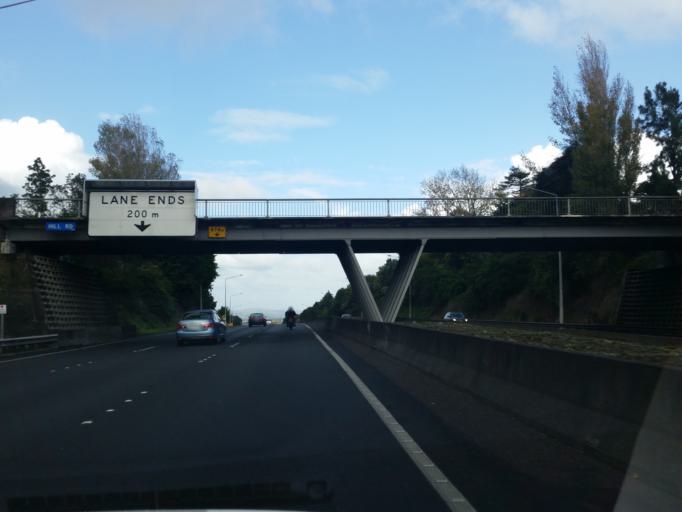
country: NZ
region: Auckland
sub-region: Auckland
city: Manukau City
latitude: -37.0142
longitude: 174.9061
